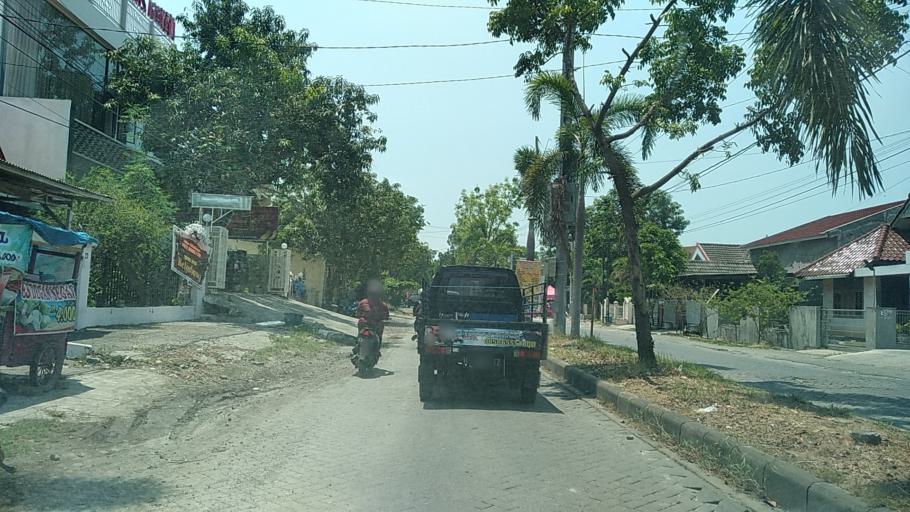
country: ID
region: Central Java
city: Semarang
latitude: -6.9811
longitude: 110.4651
